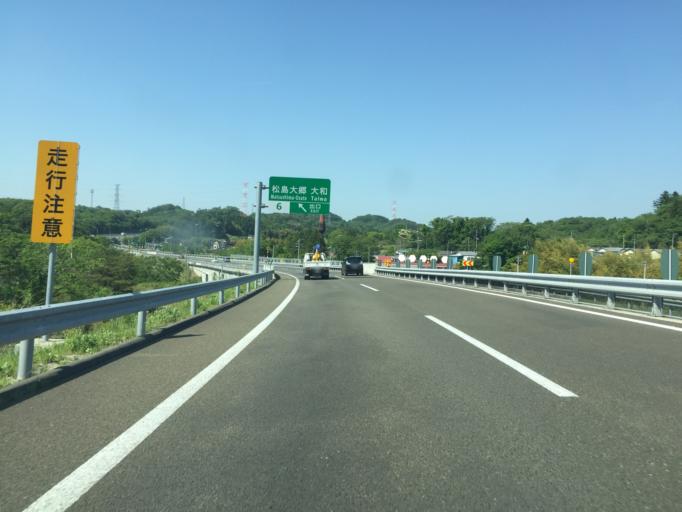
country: JP
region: Miyagi
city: Matsushima
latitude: 38.3951
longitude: 141.0411
